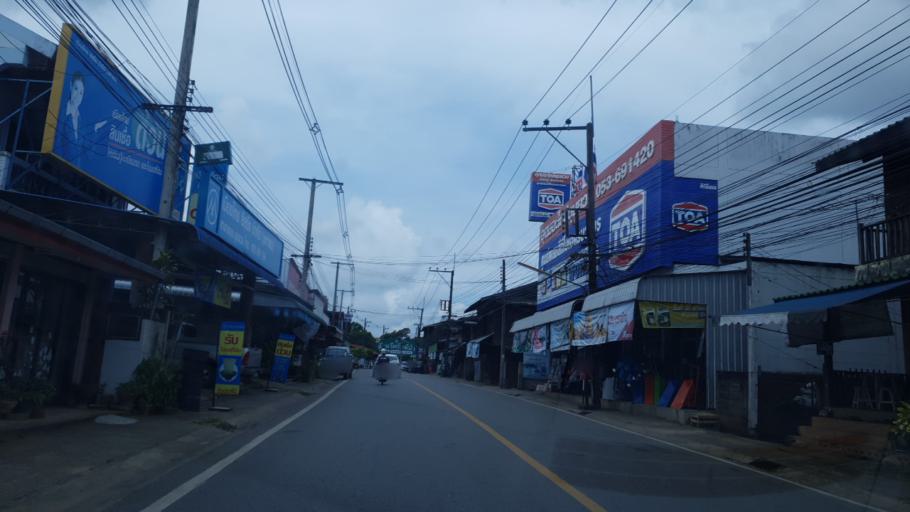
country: TH
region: Mae Hong Son
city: Khun Yuam
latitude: 18.8262
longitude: 97.9334
